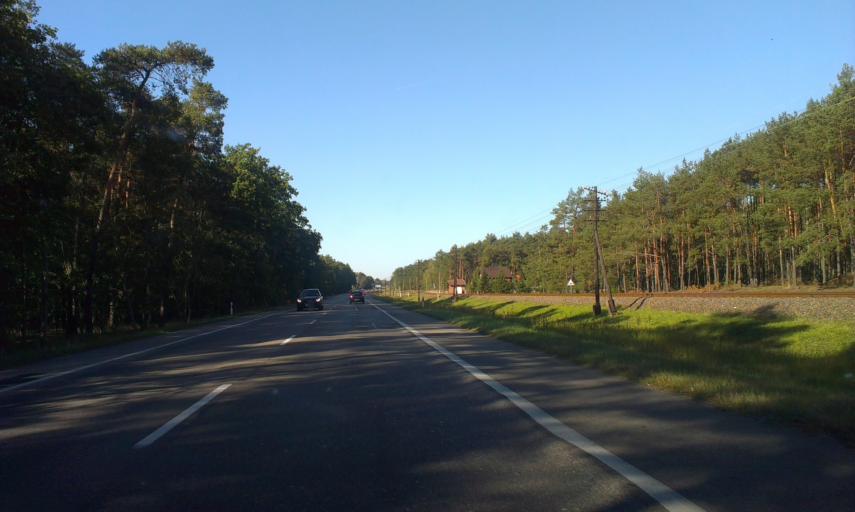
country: PL
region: Kujawsko-Pomorskie
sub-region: Powiat torunski
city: Lysomice
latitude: 53.0635
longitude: 18.6176
